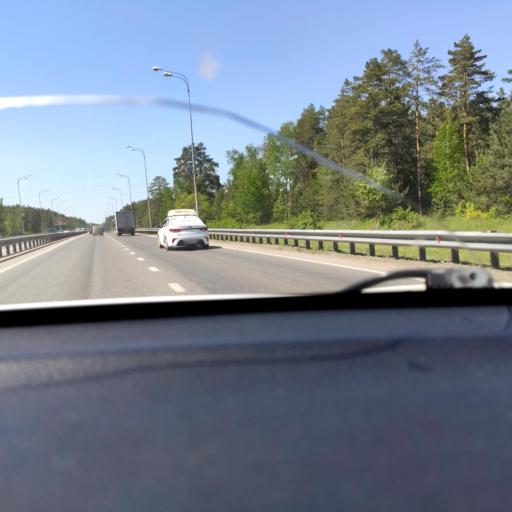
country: RU
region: Tatarstan
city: Staroye Arakchino
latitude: 55.8288
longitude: 49.0119
